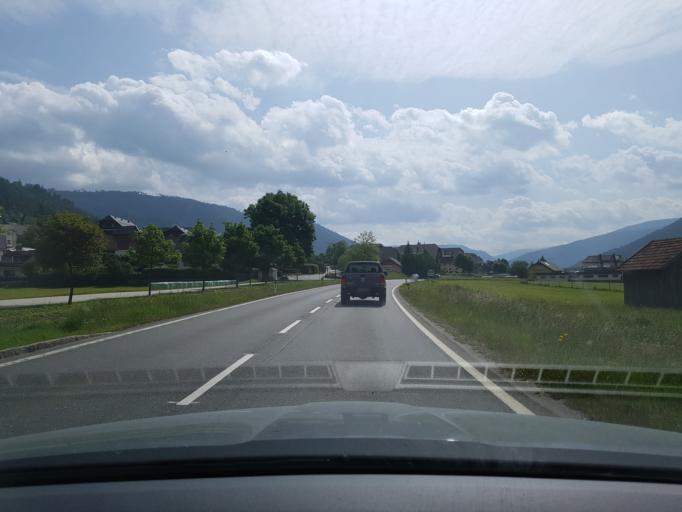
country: AT
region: Salzburg
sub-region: Politischer Bezirk Tamsweg
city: Sankt Michael im Lungau
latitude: 47.0979
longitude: 13.6283
